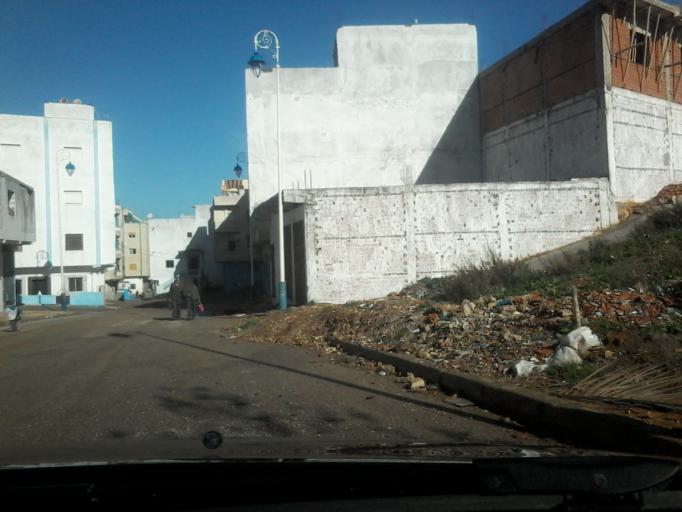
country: MA
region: Tanger-Tetouan
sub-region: Tetouan
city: Martil
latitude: 35.6773
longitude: -5.3269
